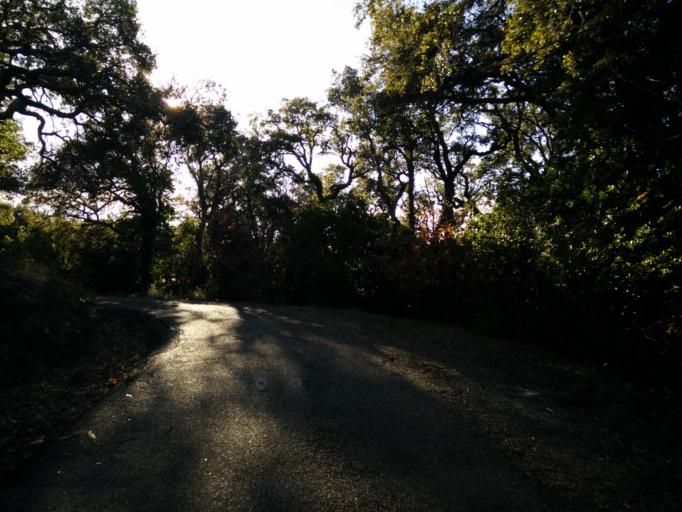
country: FR
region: Provence-Alpes-Cote d'Azur
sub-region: Departement du Var
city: Collobrieres
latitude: 43.2680
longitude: 6.2907
